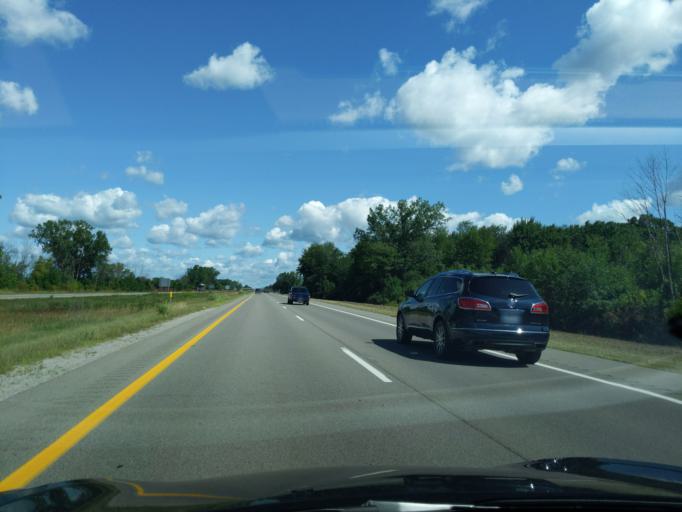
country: US
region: Michigan
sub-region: Gratiot County
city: Alma
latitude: 43.4241
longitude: -84.6771
